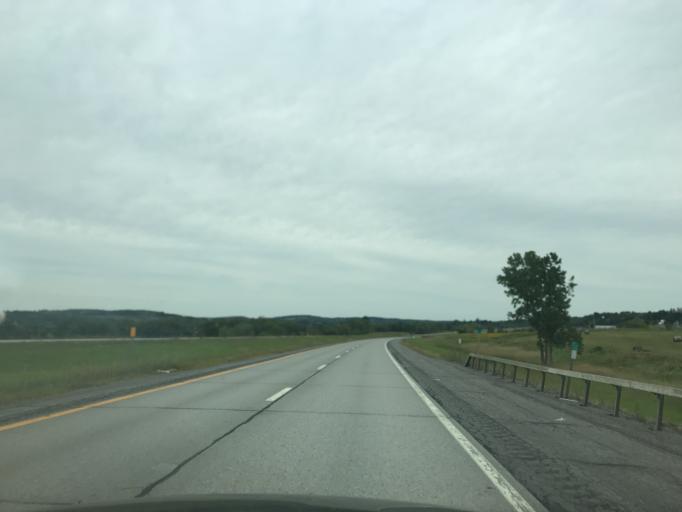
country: US
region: New York
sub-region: Schoharie County
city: Cobleskill
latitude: 42.6687
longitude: -74.4875
